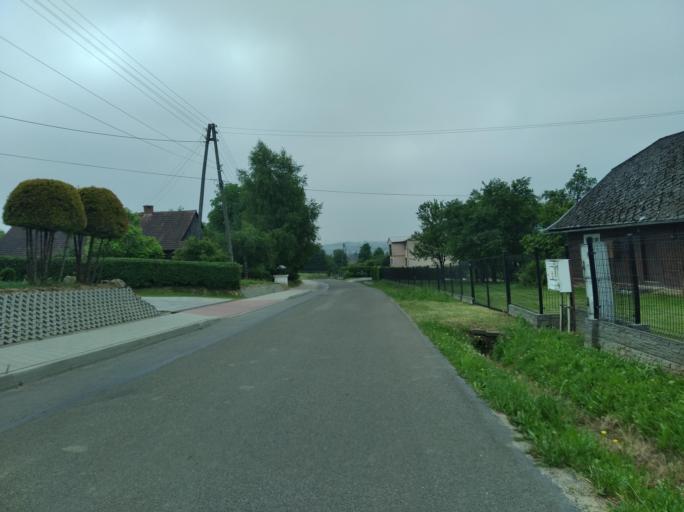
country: PL
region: Subcarpathian Voivodeship
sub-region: Powiat brzozowski
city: Jablonica Polska
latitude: 49.7045
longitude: 21.8930
